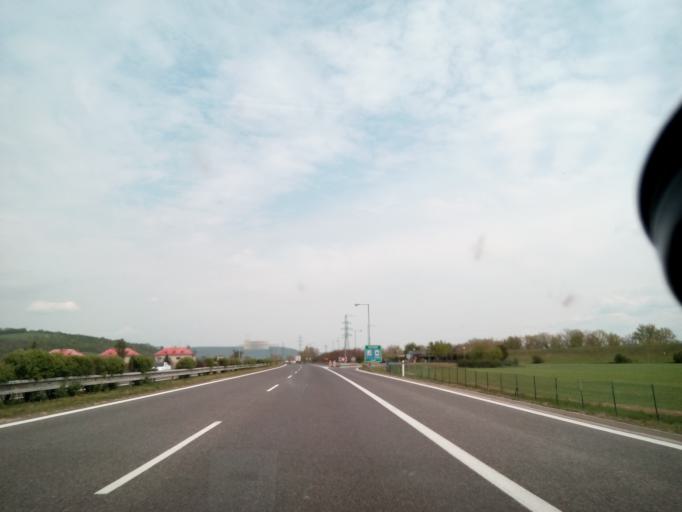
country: SK
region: Trenciansky
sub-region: Okres Trencin
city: Trencin
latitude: 48.8672
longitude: 17.9667
